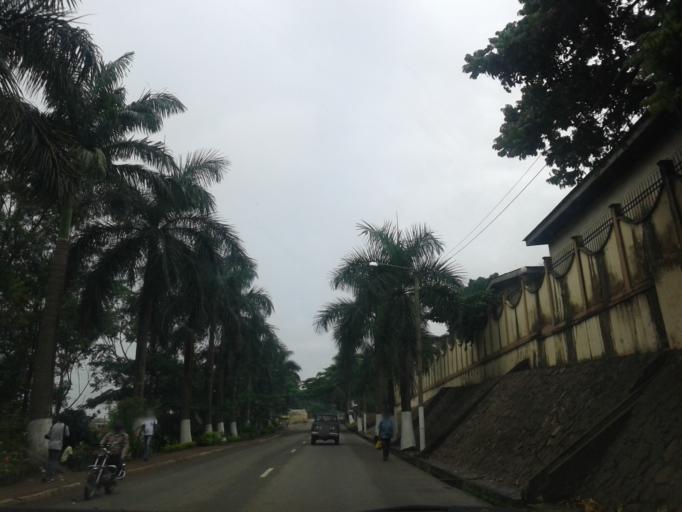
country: CM
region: Centre
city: Yaounde
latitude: 3.8769
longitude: 11.5142
